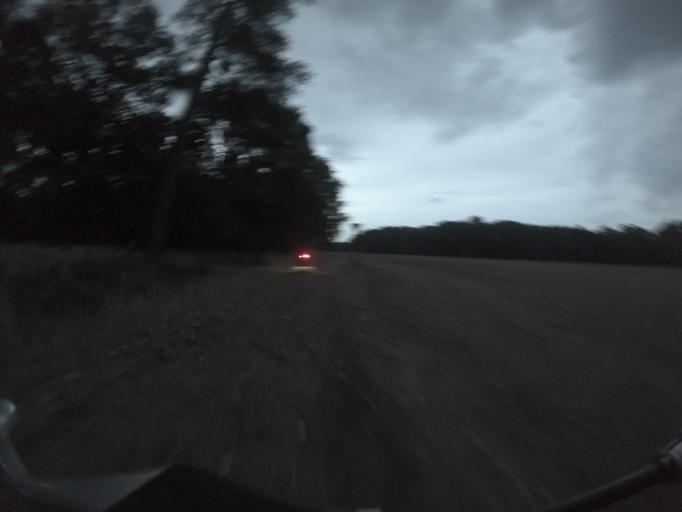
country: DE
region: Hesse
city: Morfelden-Walldorf
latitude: 49.9992
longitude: 8.5486
